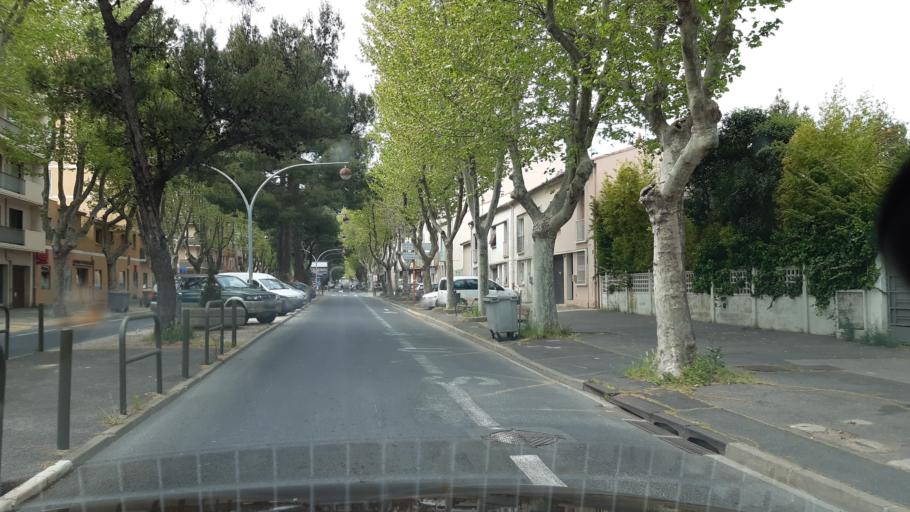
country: FR
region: Languedoc-Roussillon
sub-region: Departement de l'Aude
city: Narbonne
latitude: 43.1917
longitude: 3.0150
